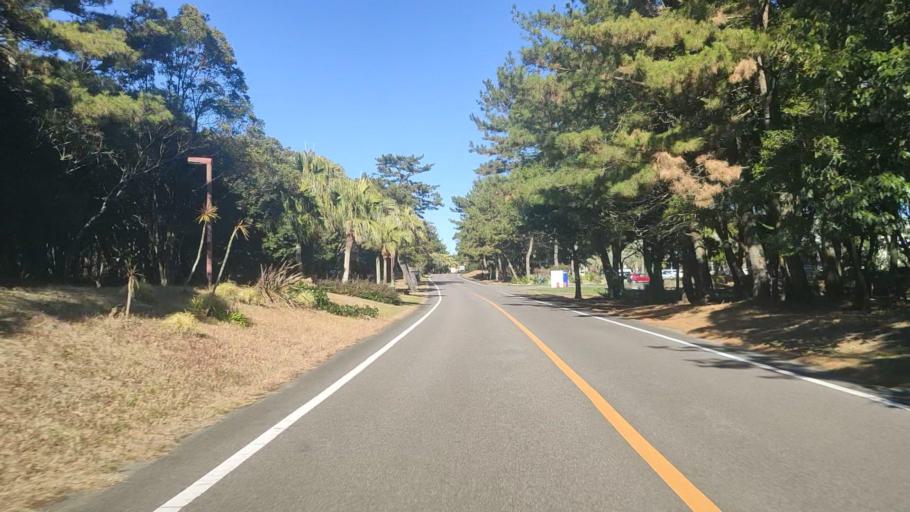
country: JP
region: Miyazaki
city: Miyazaki-shi
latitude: 31.9508
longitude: 131.4663
